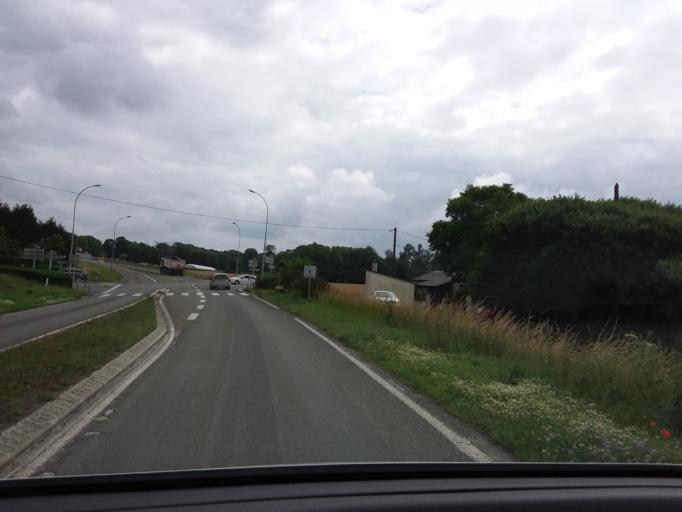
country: FR
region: Picardie
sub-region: Departement de l'Aisne
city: Bucy-le-Long
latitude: 49.3841
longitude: 3.4401
